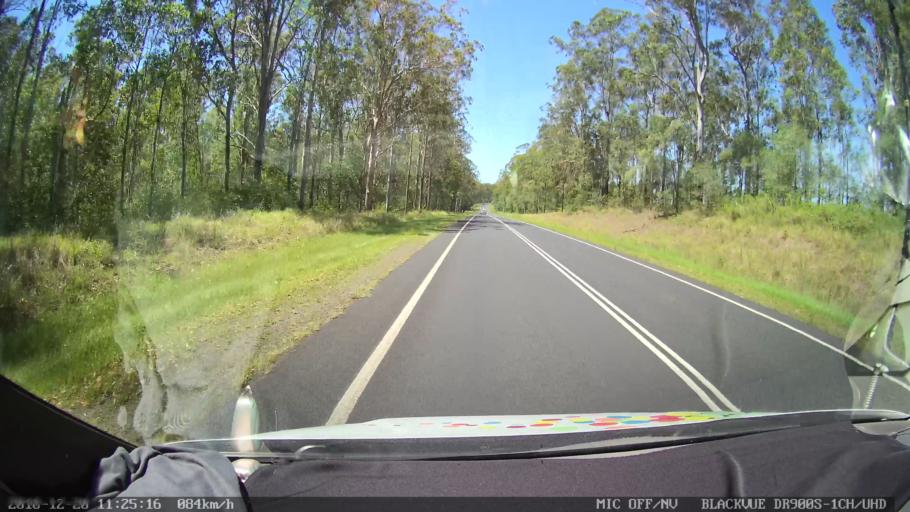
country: AU
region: New South Wales
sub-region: Richmond Valley
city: Casino
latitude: -29.0853
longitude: 153.0008
